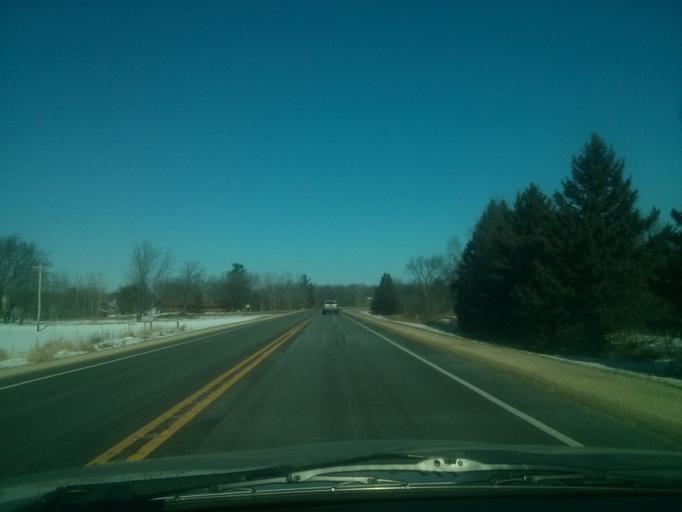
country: US
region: Wisconsin
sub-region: Polk County
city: Clear Lake
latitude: 45.1713
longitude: -92.2833
